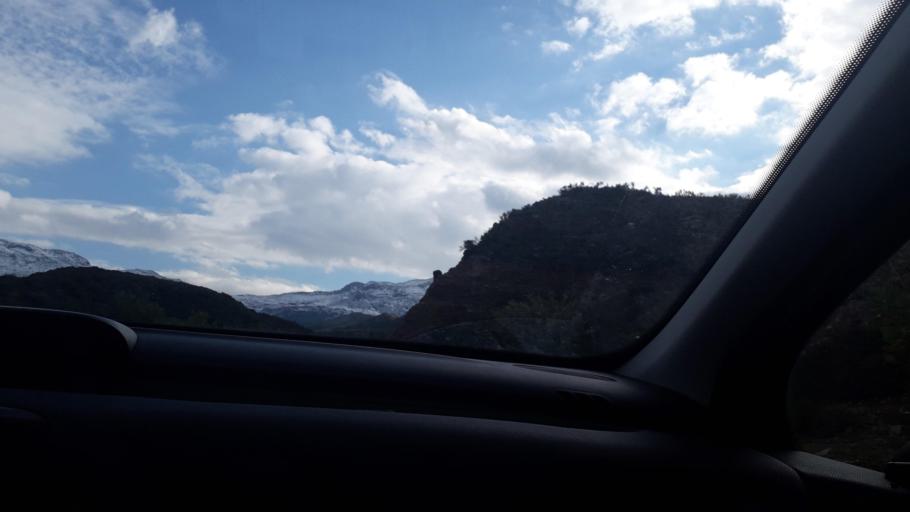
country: GR
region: Crete
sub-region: Nomos Rethymnis
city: Agia Foteini
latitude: 35.2806
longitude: 24.5622
